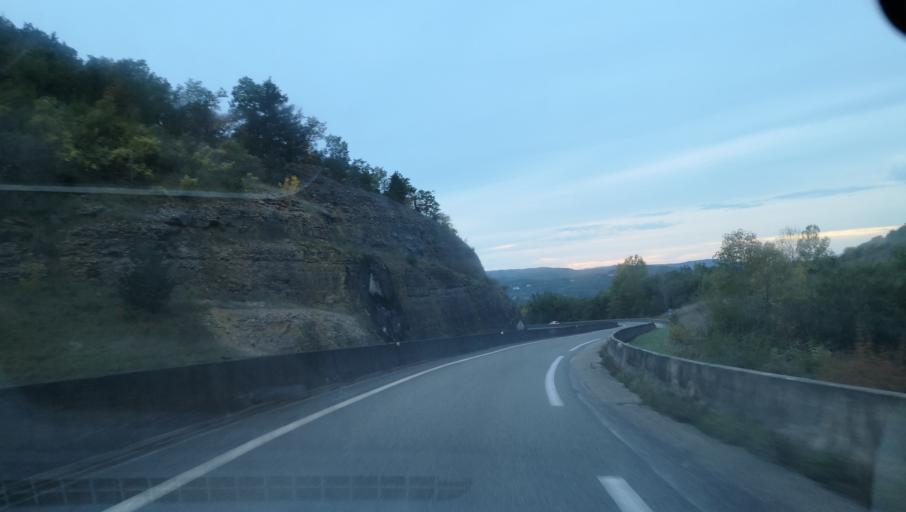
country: FR
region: Midi-Pyrenees
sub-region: Departement du Lot
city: Cahors
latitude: 44.4777
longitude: 1.4359
